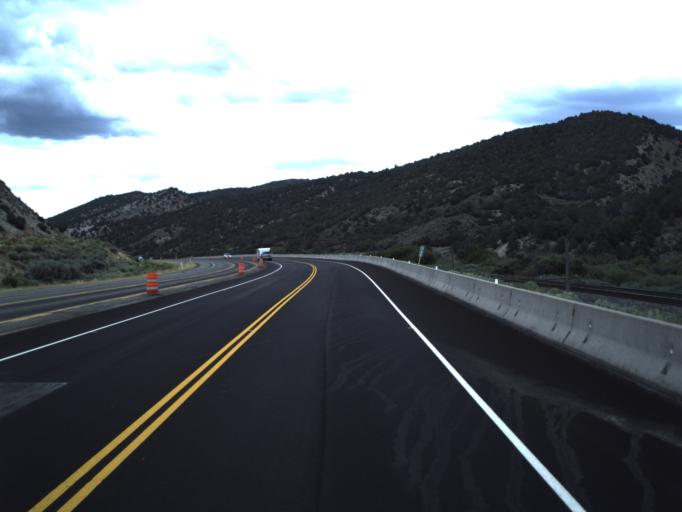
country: US
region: Utah
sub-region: Utah County
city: Mapleton
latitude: 39.9528
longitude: -111.2912
